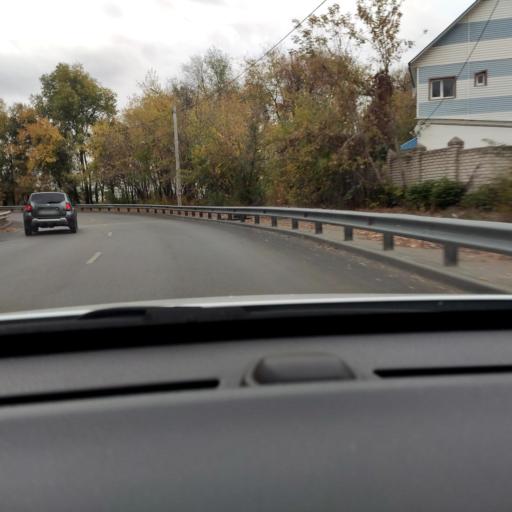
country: RU
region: Voronezj
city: Voronezh
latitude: 51.7083
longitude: 39.2262
